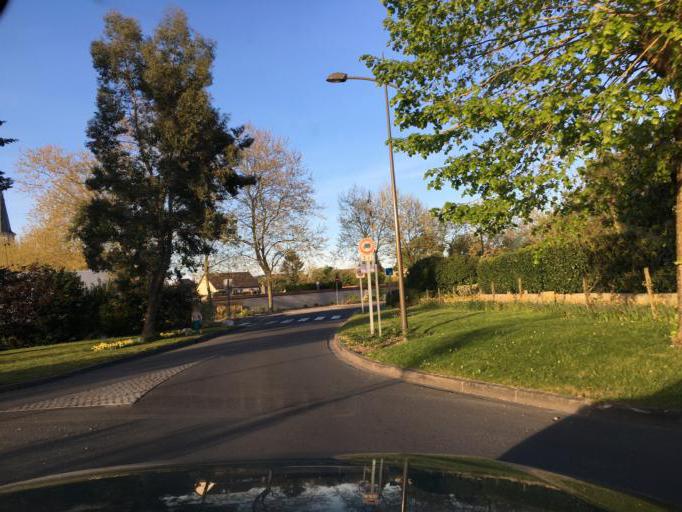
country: FR
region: Centre
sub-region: Departement du Loiret
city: Saint-Denis-en-Val
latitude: 47.8773
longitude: 1.9548
